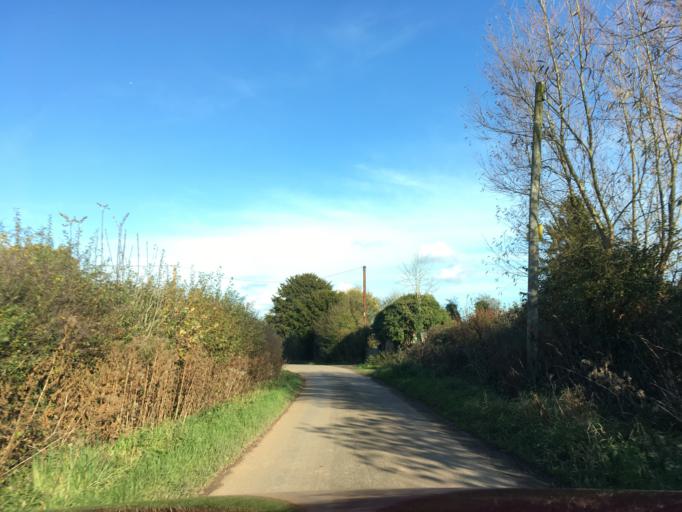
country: GB
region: England
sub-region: South Gloucestershire
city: Falfield
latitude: 51.6502
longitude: -2.4717
